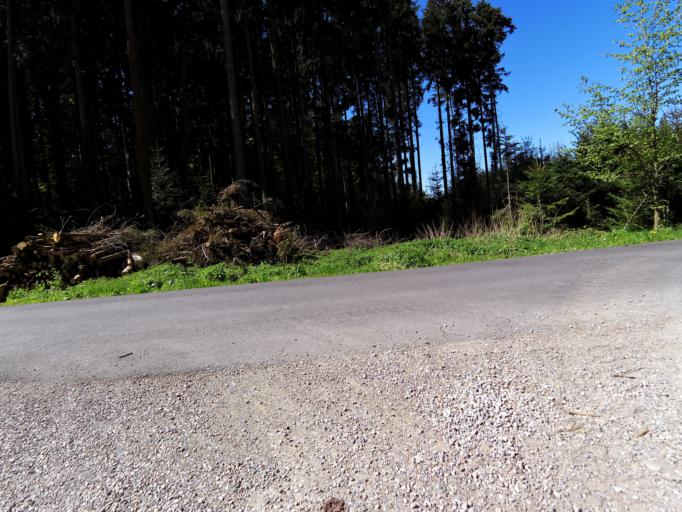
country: CH
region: Thurgau
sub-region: Weinfelden District
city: Berg
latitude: 47.5834
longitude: 9.1476
